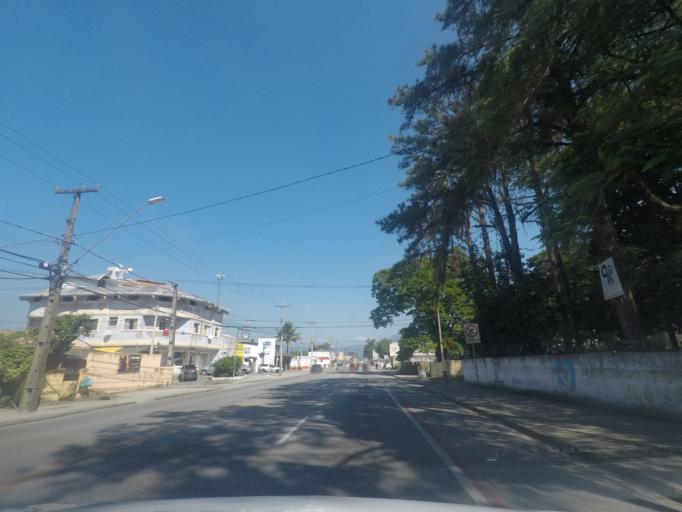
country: BR
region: Parana
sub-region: Paranagua
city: Paranagua
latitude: -25.5493
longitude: -48.5465
